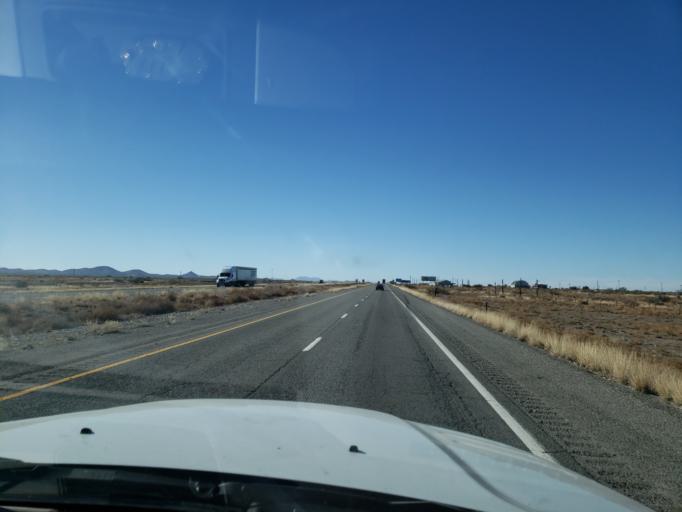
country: US
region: New Mexico
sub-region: Hidalgo County
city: Lordsburg
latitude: 32.3327
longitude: -108.6506
